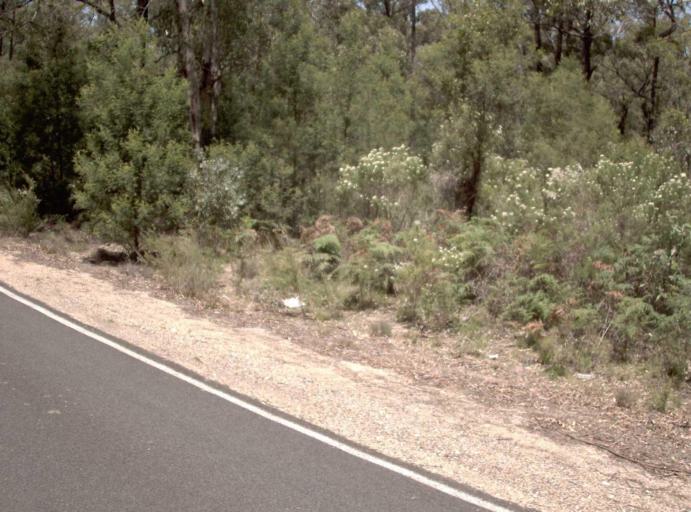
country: AU
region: Victoria
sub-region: East Gippsland
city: Lakes Entrance
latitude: -37.6347
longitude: 147.8961
